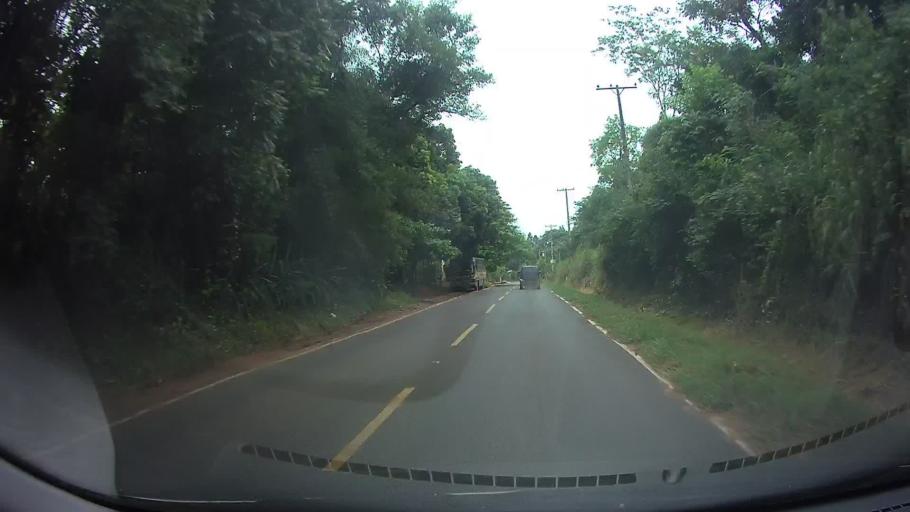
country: PY
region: Central
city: Itaugua
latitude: -25.3566
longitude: -57.3437
